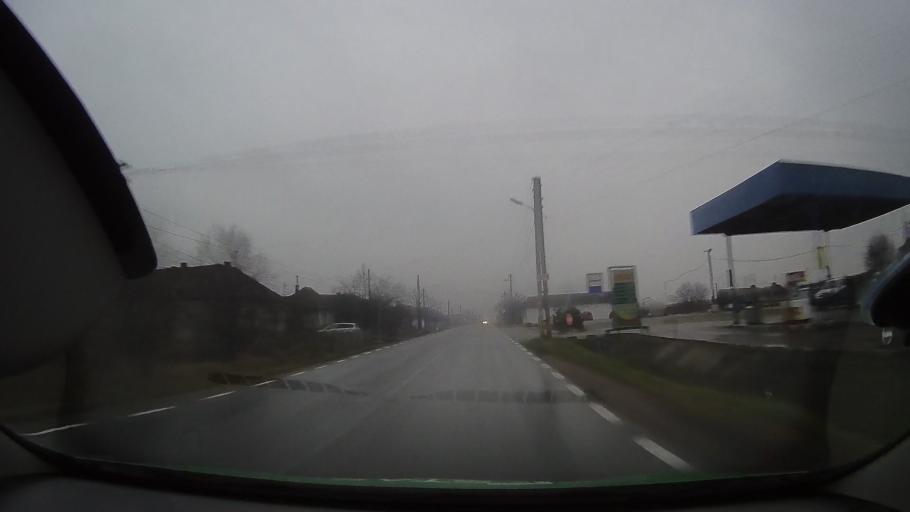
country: RO
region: Bihor
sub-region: Comuna Tinca
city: Tinca
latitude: 46.7379
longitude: 21.9412
